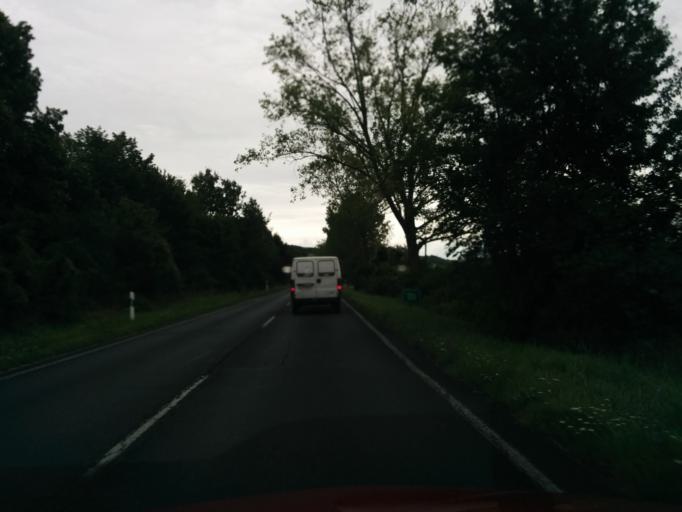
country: AT
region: Burgenland
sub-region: Eisenstadt-Umgebung
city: Klingenbach
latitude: 47.7223
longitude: 16.5638
